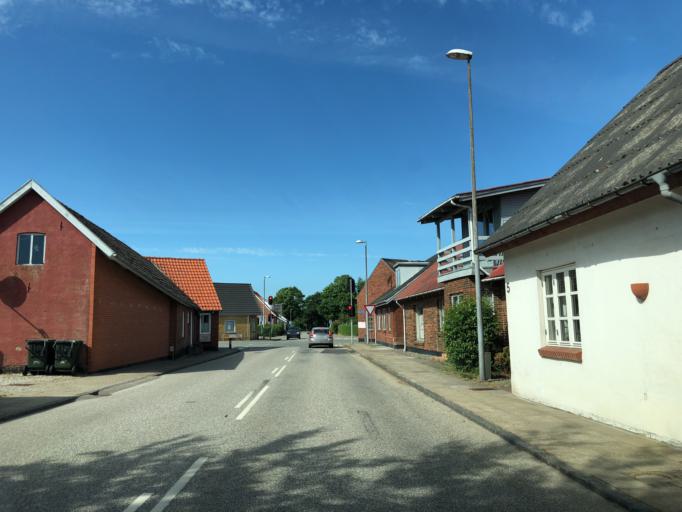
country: DK
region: Central Jutland
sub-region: Herning Kommune
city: Snejbjerg
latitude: 56.1306
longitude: 8.8895
